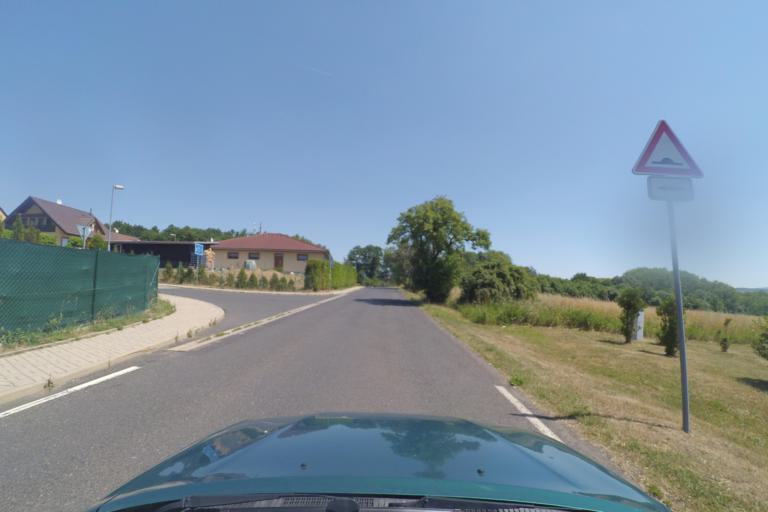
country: CZ
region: Ustecky
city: Chlumec
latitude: 50.6942
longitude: 13.9265
